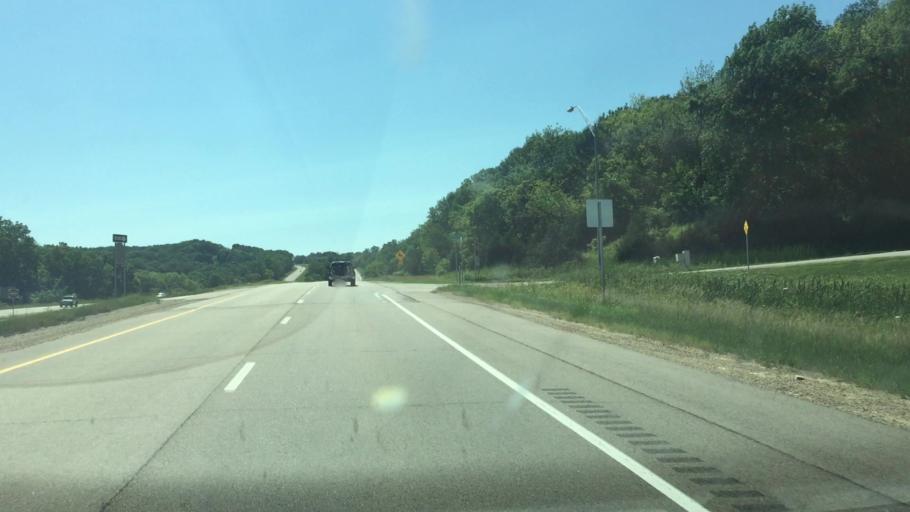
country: US
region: Iowa
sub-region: Dubuque County
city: Dubuque
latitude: 42.4189
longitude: -90.7028
